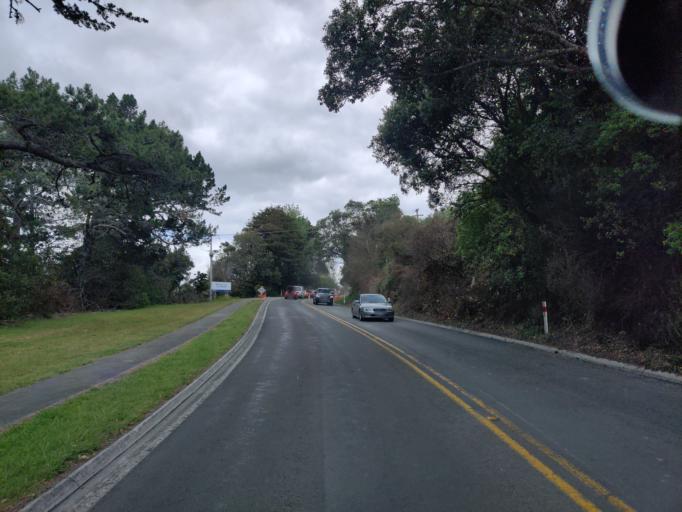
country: NZ
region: Northland
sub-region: Far North District
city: Taipa
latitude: -34.9913
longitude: 173.4767
